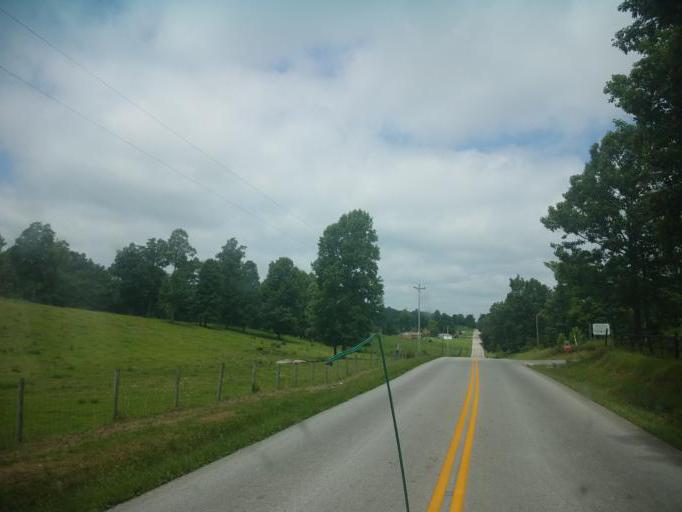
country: US
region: Kentucky
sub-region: Hart County
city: Munfordville
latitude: 37.3041
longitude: -85.9417
